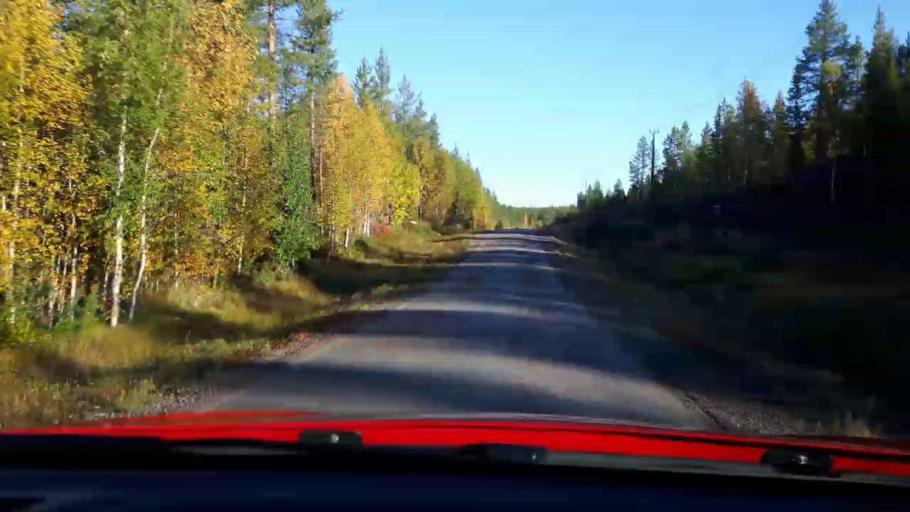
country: SE
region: Jaemtland
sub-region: Stroemsunds Kommun
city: Stroemsund
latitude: 64.3760
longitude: 15.1506
